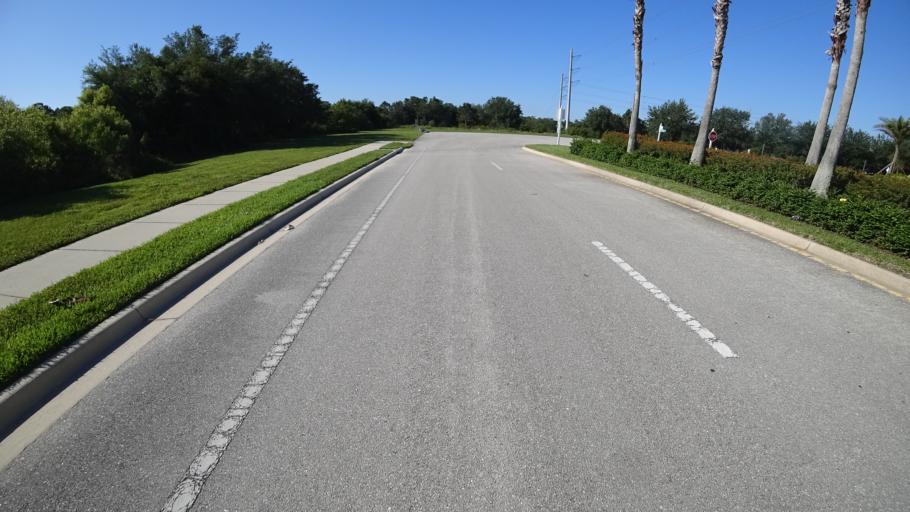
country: US
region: Florida
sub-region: Sarasota County
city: The Meadows
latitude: 27.3872
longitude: -82.3528
